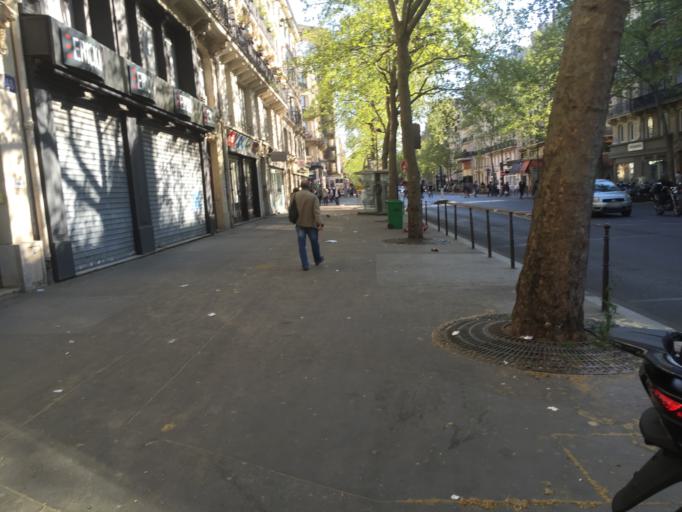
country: FR
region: Ile-de-France
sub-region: Paris
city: Paris
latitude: 48.8626
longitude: 2.3504
